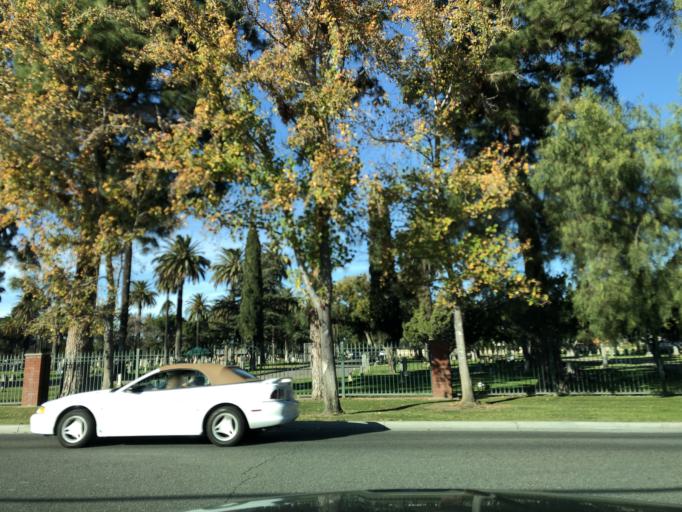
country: US
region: California
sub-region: Orange County
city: Tustin
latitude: 33.7671
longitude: -117.8387
